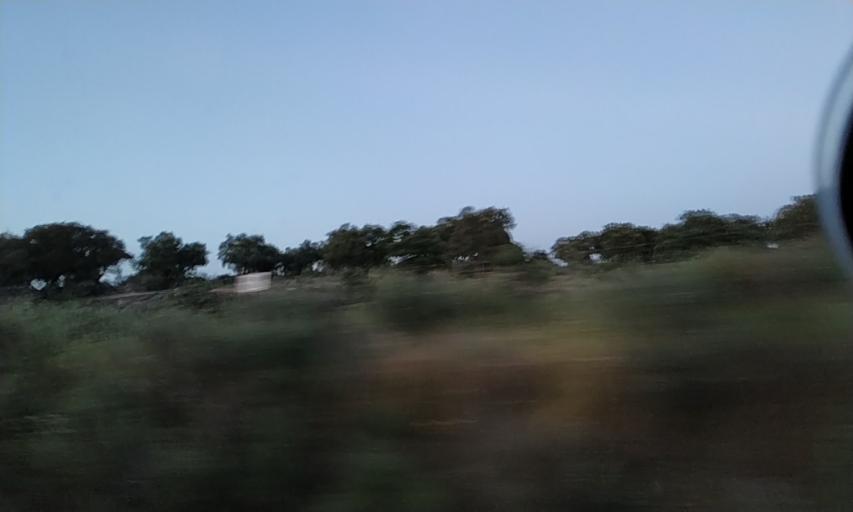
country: ES
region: Extremadura
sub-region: Provincia de Caceres
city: Piedras Albas
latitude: 39.7612
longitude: -6.9064
